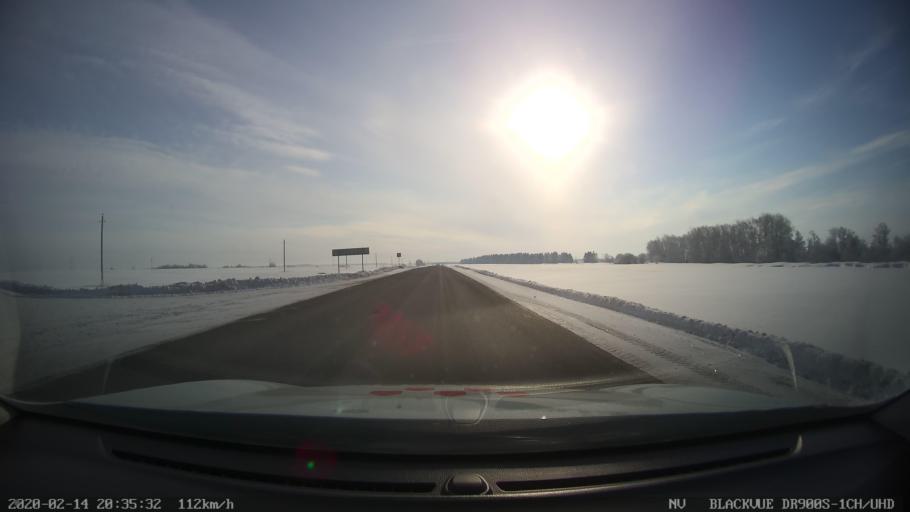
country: RU
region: Tatarstan
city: Kuybyshevskiy Zaton
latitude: 55.3810
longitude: 48.9854
